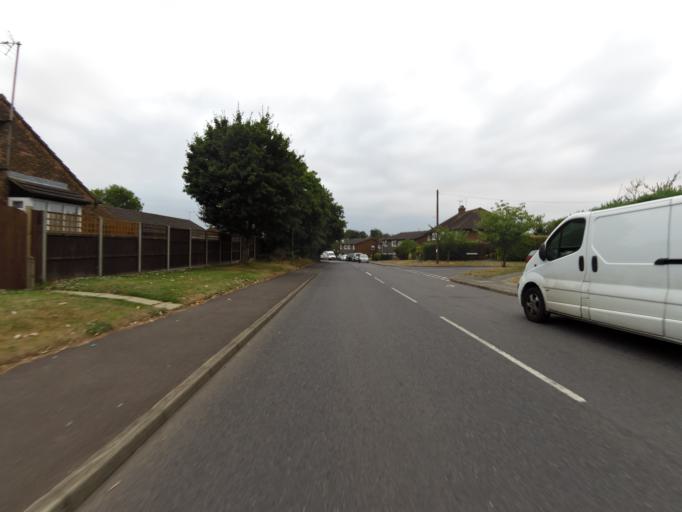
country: GB
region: England
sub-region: Hertfordshire
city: Shenley AV
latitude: 51.7205
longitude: -0.2946
